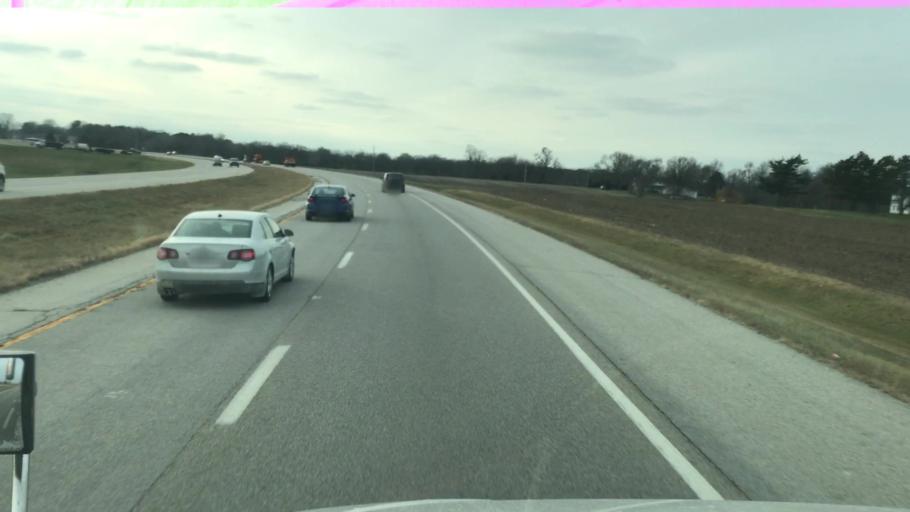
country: US
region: Illinois
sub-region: Warren County
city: Monmouth
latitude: 40.9258
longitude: -90.6537
